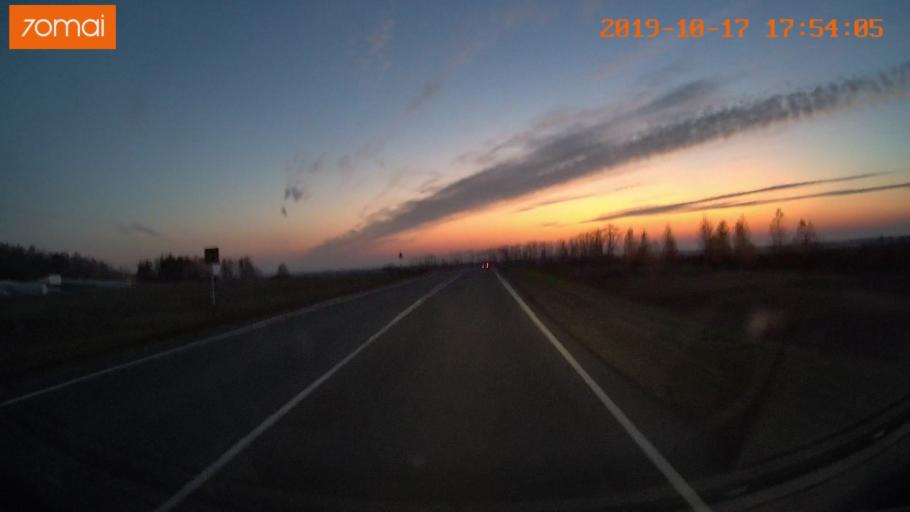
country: RU
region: Tula
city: Kurkino
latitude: 53.6107
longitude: 38.6713
